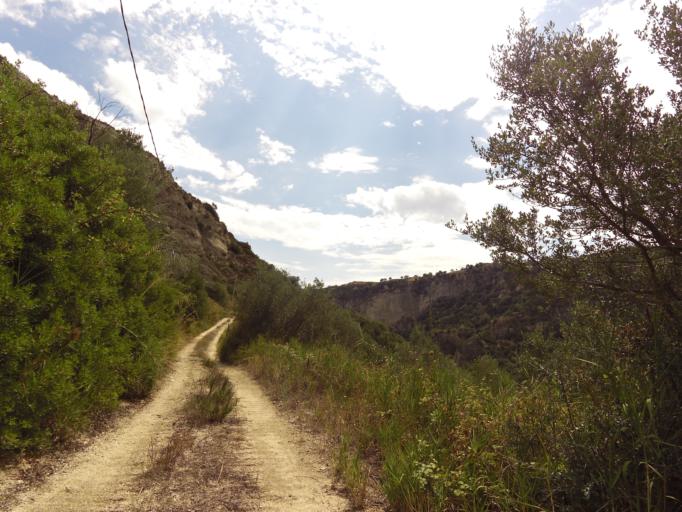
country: IT
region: Calabria
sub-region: Provincia di Reggio Calabria
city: Camini
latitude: 38.4527
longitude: 16.4742
